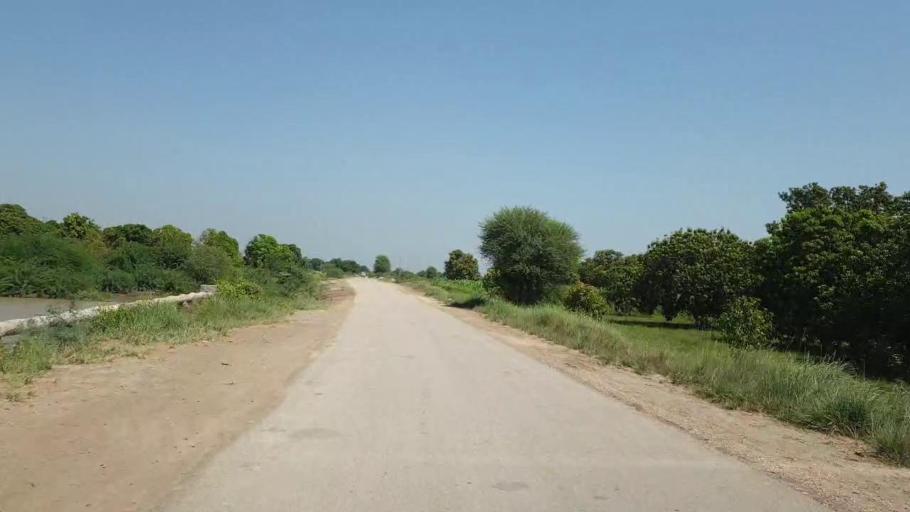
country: PK
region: Sindh
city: Hyderabad
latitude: 25.4593
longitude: 68.4240
